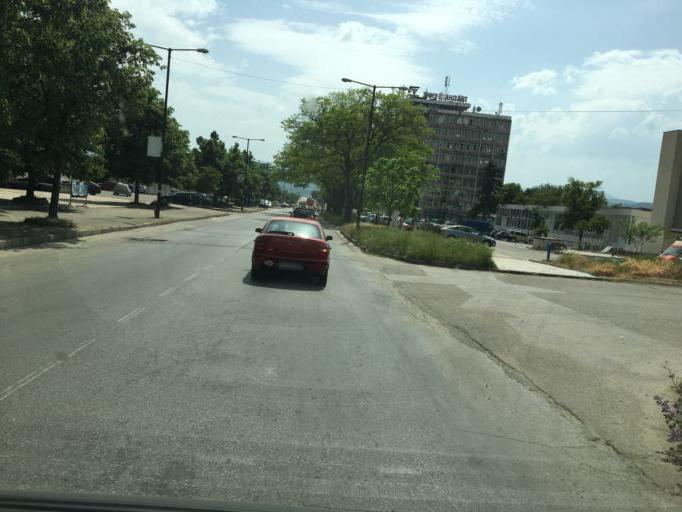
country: BG
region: Blagoevgrad
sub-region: Obshtina Blagoevgrad
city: Blagoevgrad
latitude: 42.0077
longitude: 23.0856
